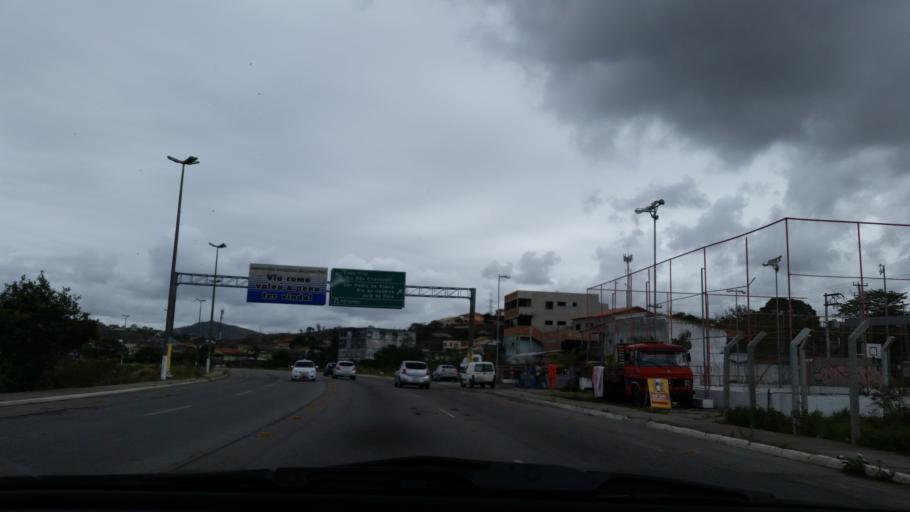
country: BR
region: Rio de Janeiro
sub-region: Cabo Frio
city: Cabo Frio
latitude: -22.8568
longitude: -42.0382
